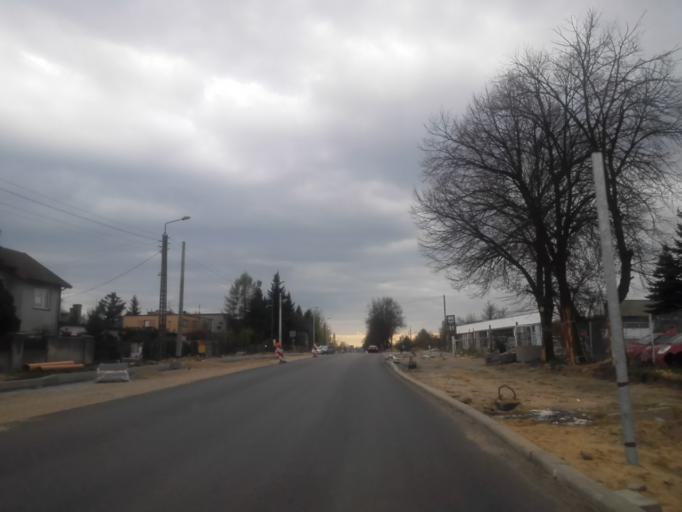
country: PL
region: Silesian Voivodeship
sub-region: Czestochowa
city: Czestochowa
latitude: 50.8371
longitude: 19.1554
